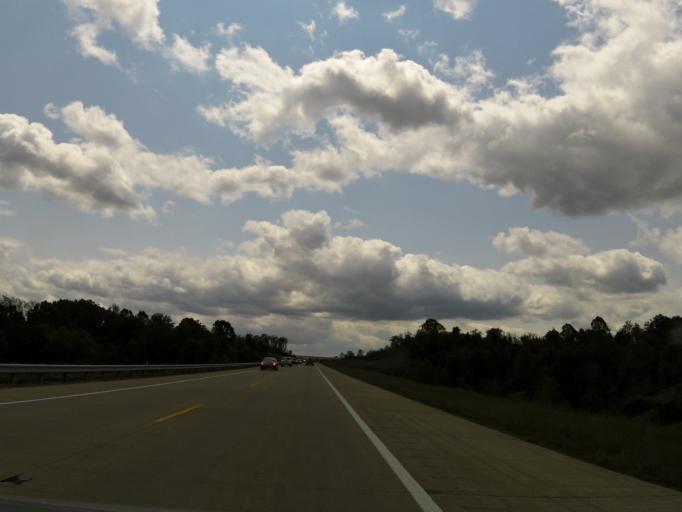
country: US
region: Ohio
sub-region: Athens County
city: Athens
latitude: 39.2636
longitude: -82.0840
